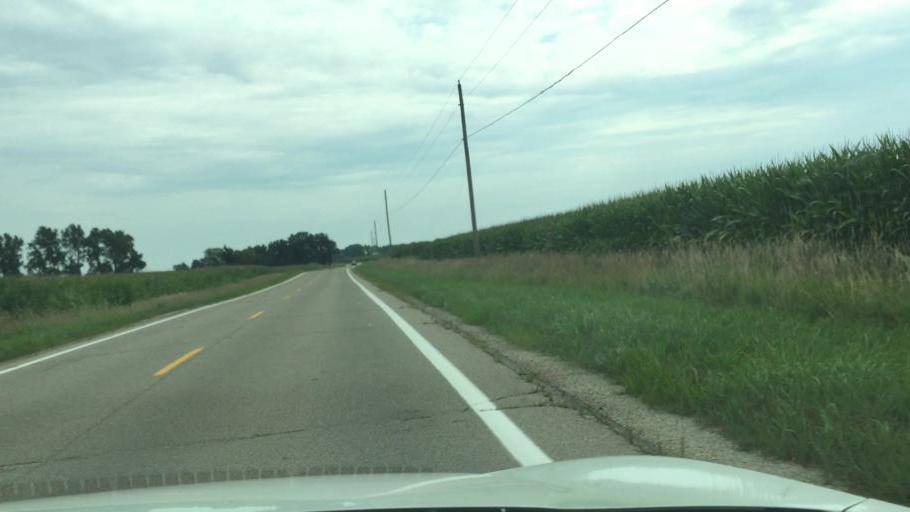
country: US
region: Ohio
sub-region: Champaign County
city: North Lewisburg
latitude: 40.1553
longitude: -83.5280
